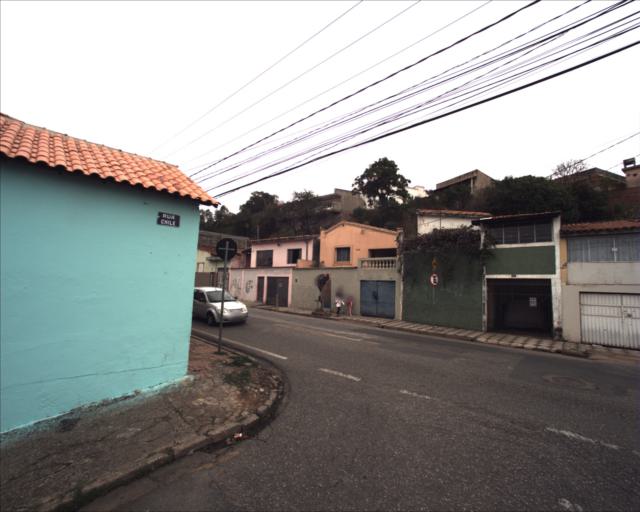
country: BR
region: Sao Paulo
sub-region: Sorocaba
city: Sorocaba
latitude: -23.5211
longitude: -47.4421
